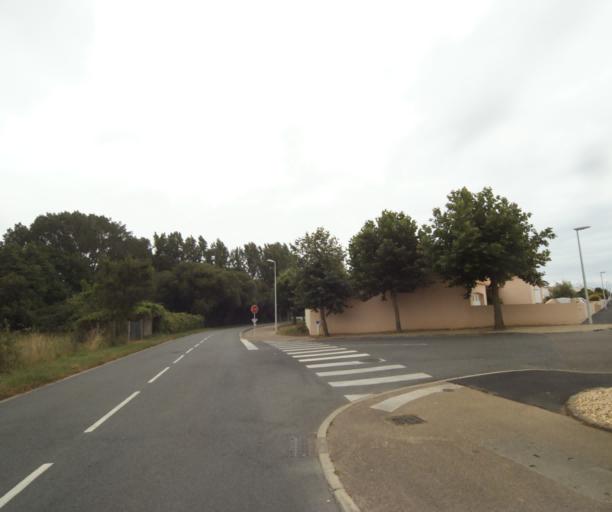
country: FR
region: Pays de la Loire
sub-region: Departement de la Vendee
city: Chateau-d'Olonne
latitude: 46.5004
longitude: -1.7416
